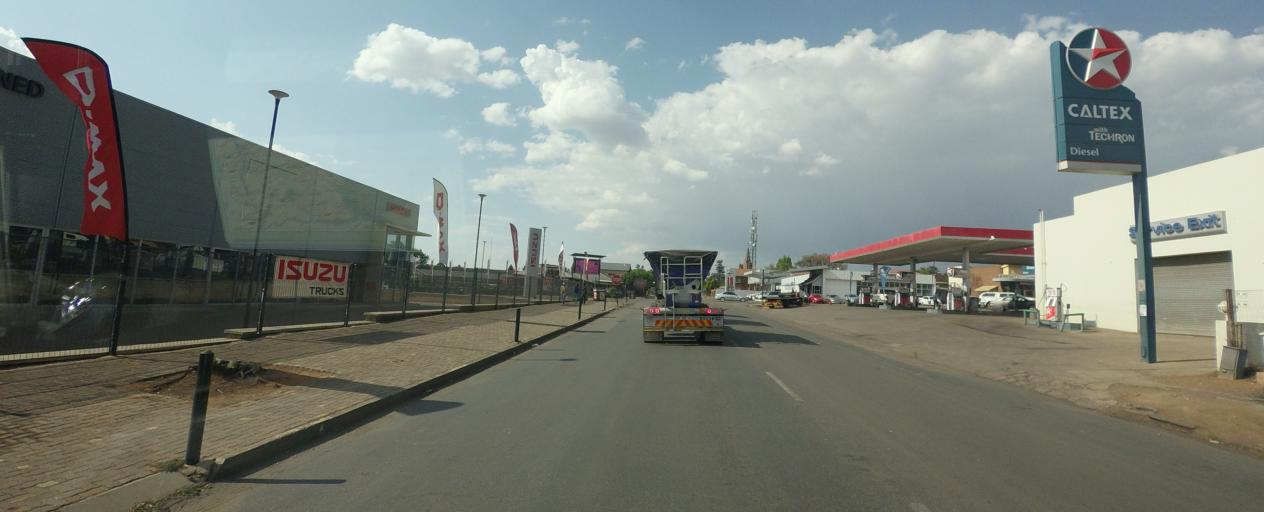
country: ZA
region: Mpumalanga
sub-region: Ehlanzeni District
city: Lydenburg
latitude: -25.0963
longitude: 30.4552
